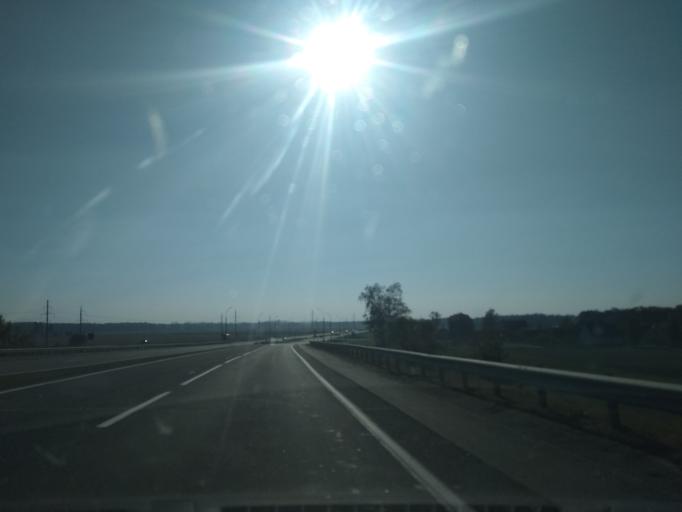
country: BY
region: Brest
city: Horad Kobryn
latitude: 52.2050
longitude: 24.4202
